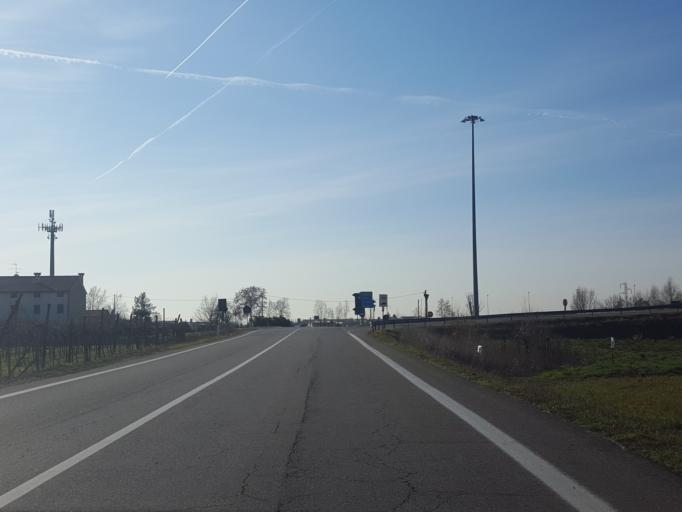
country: IT
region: Veneto
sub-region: Provincia di Vicenza
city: Lonigo
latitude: 45.3875
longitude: 11.3811
